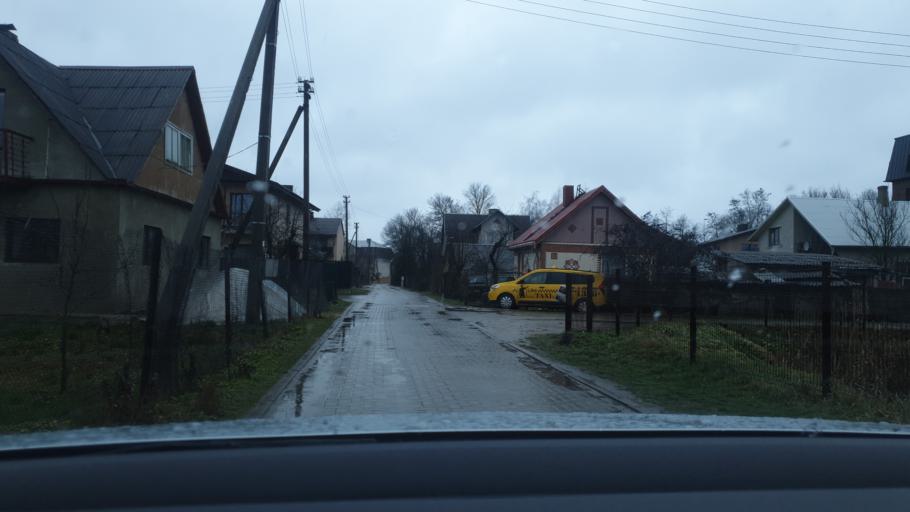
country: LT
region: Vilnius County
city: Rasos
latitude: 54.6638
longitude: 25.3455
